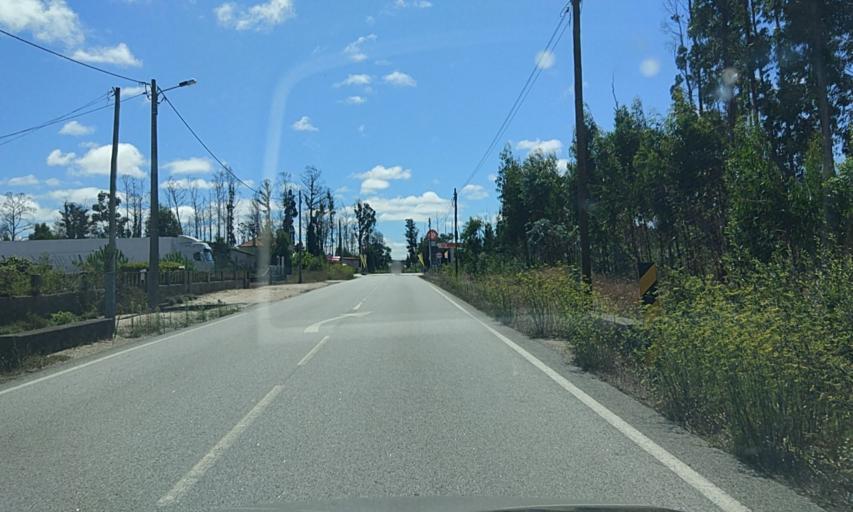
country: PT
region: Coimbra
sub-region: Mira
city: Mira
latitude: 40.4077
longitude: -8.7354
